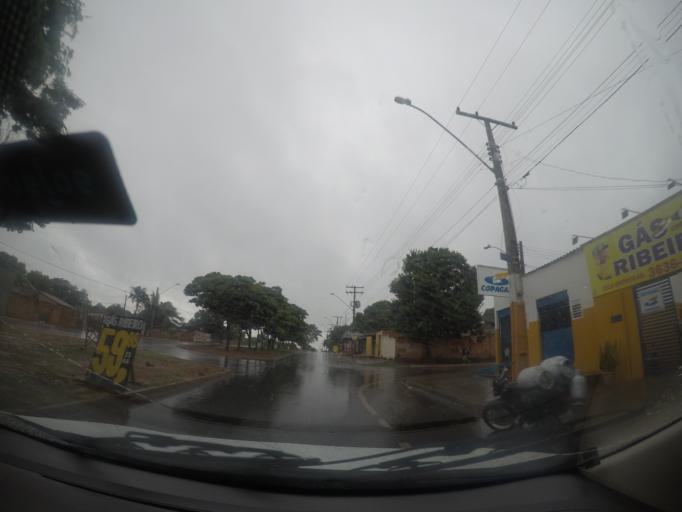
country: BR
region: Goias
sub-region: Goiania
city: Goiania
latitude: -16.5945
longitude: -49.3367
